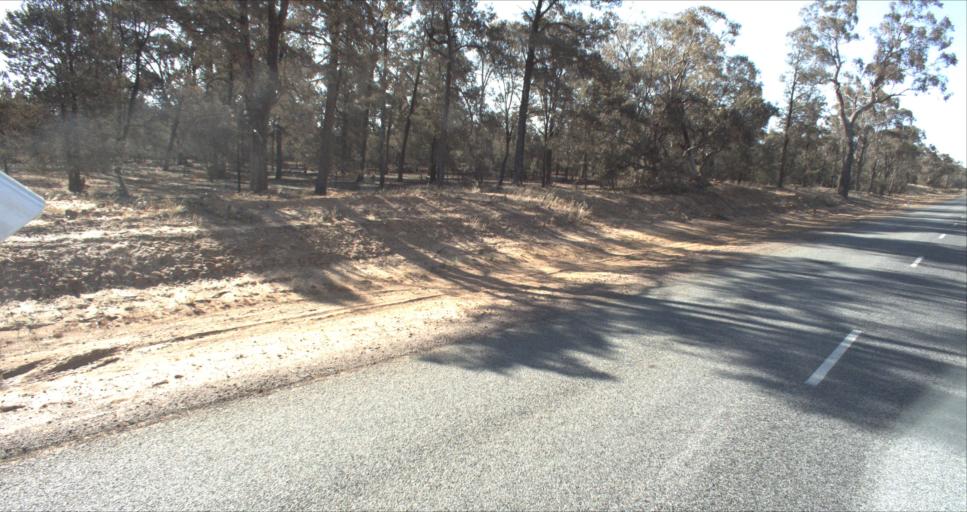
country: AU
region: New South Wales
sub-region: Leeton
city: Leeton
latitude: -34.6517
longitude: 146.3511
